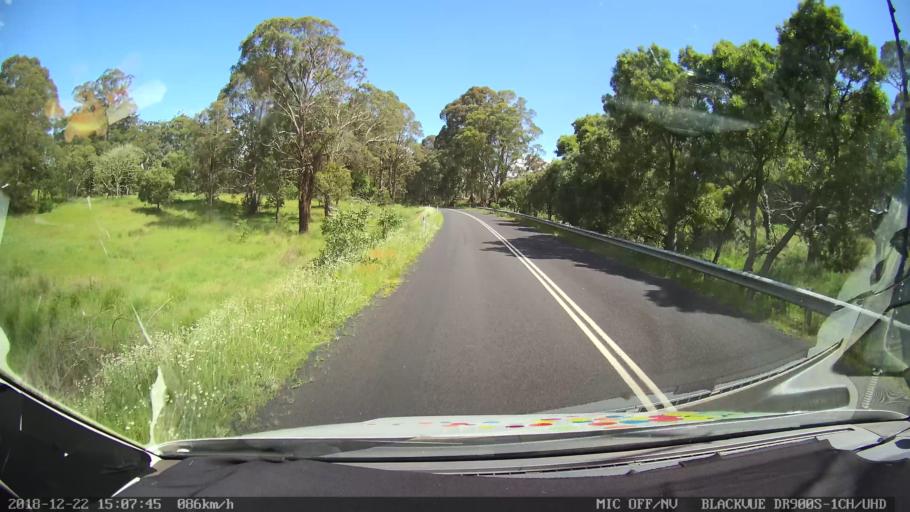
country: AU
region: New South Wales
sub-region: Bellingen
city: Dorrigo
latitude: -30.3034
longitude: 152.4125
